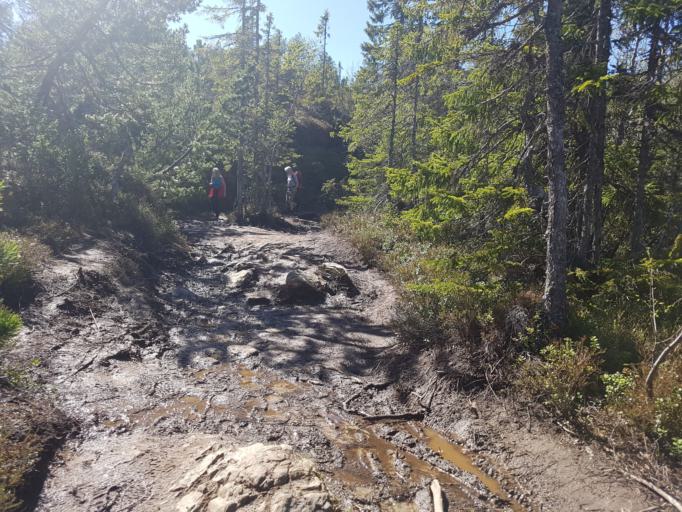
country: NO
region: Sor-Trondelag
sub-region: Trondheim
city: Trondheim
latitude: 63.4343
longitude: 10.3164
